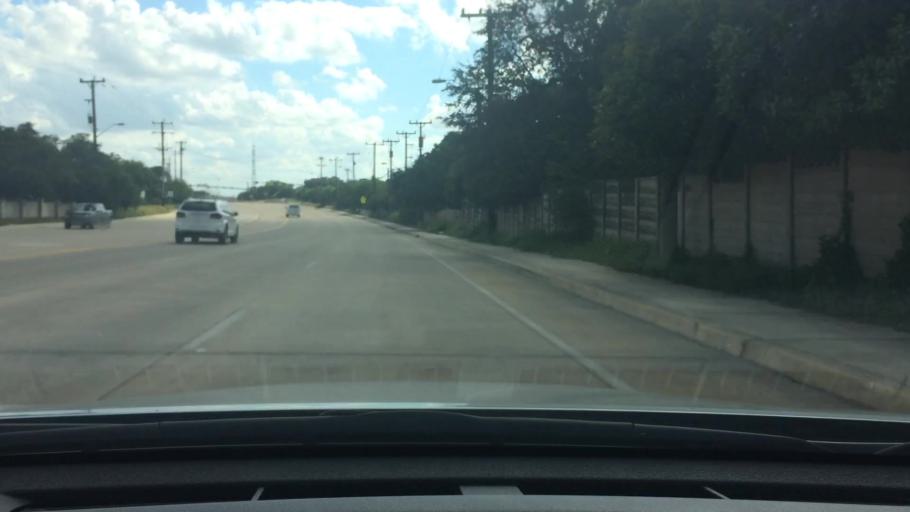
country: US
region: Texas
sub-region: Bexar County
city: Hollywood Park
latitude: 29.6417
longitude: -98.4250
